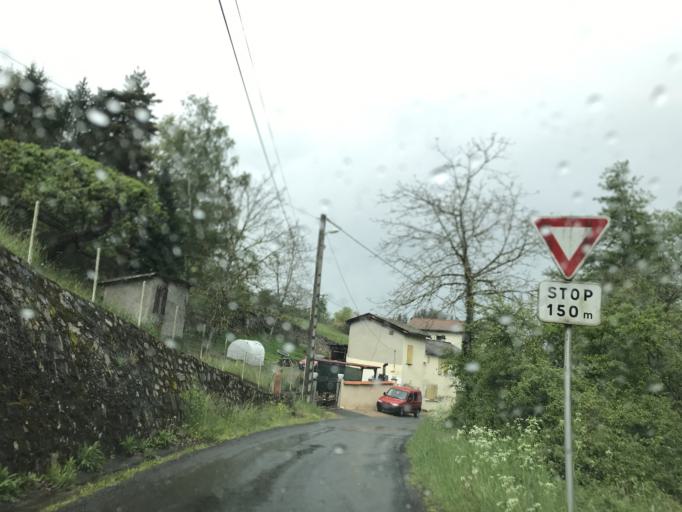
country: FR
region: Auvergne
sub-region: Departement du Puy-de-Dome
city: Courpiere
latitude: 45.7502
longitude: 3.5296
